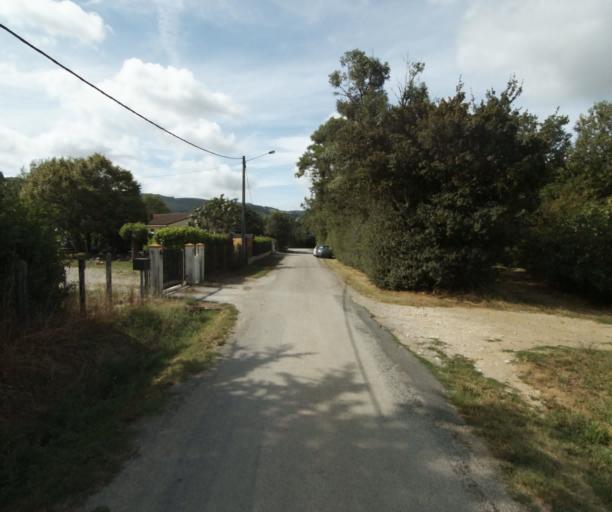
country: FR
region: Midi-Pyrenees
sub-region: Departement du Tarn
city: Soreze
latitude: 43.4738
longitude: 2.0848
